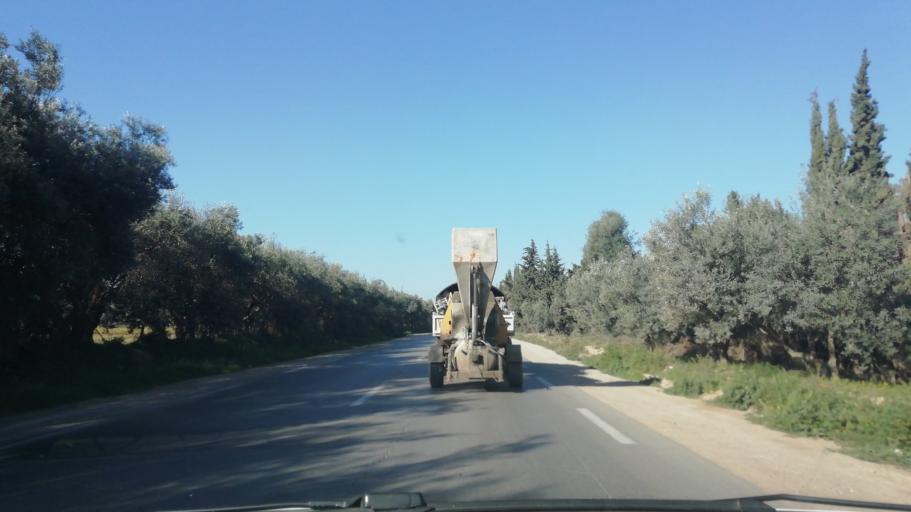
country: DZ
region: Mascara
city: Sig
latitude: 35.5662
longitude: -0.0757
